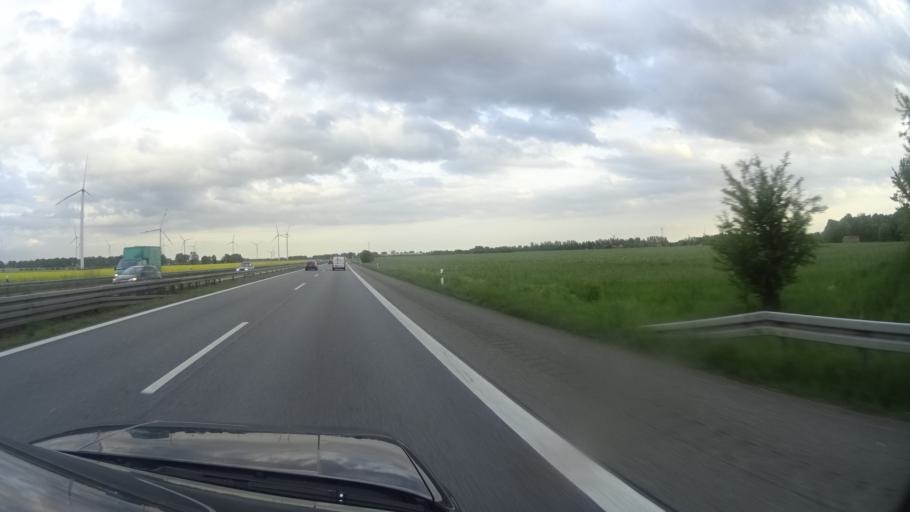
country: DE
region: Brandenburg
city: Dabergotz
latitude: 52.9253
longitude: 12.7113
